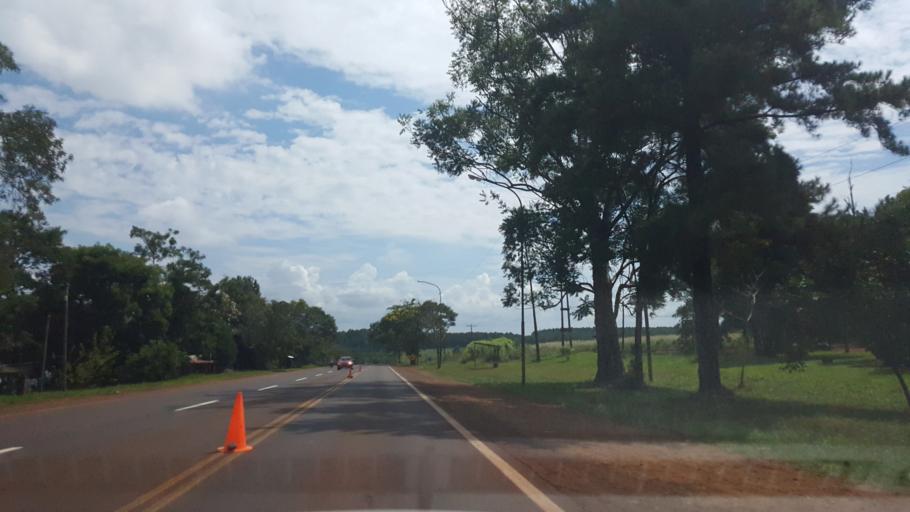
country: AR
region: Misiones
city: Capiovi
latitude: -26.9102
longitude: -55.0605
